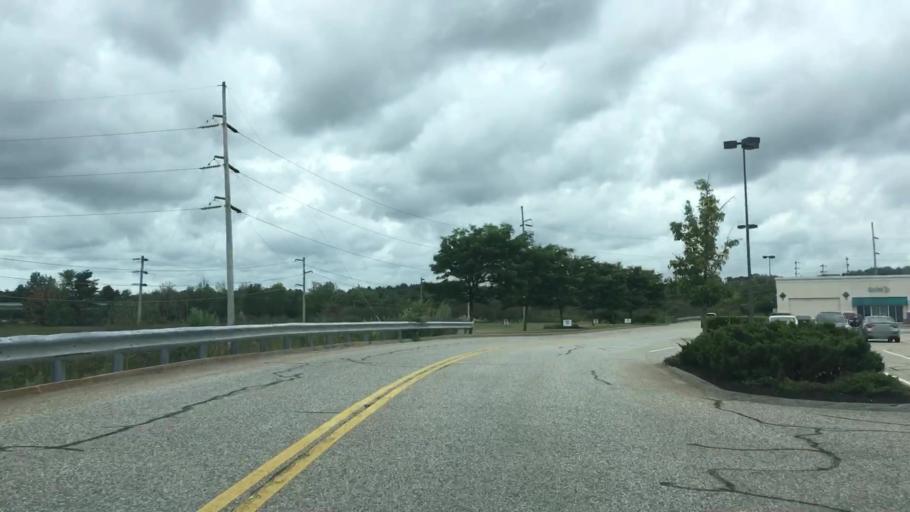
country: US
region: Maine
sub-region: Cumberland County
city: South Portland Gardens
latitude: 43.6349
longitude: -70.3437
